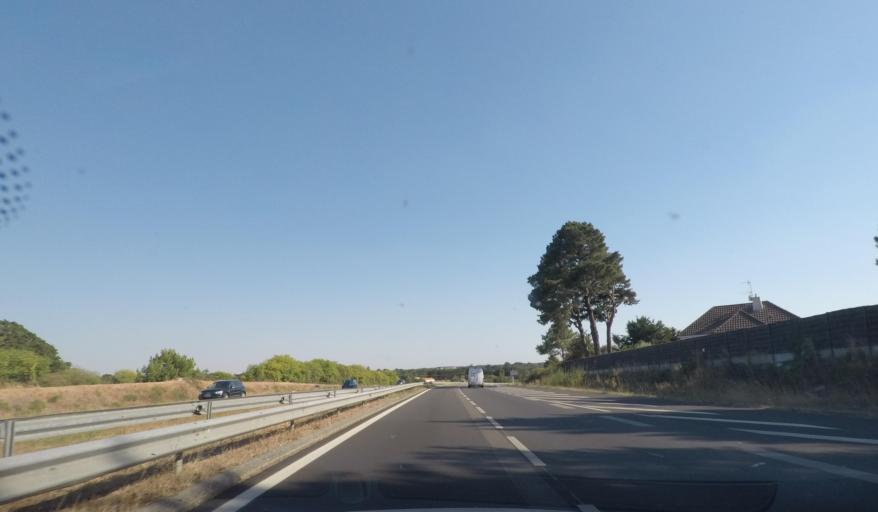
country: FR
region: Pays de la Loire
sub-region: Departement de la Loire-Atlantique
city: Saint-Michel-Chef-Chef
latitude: 47.1830
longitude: -2.1459
